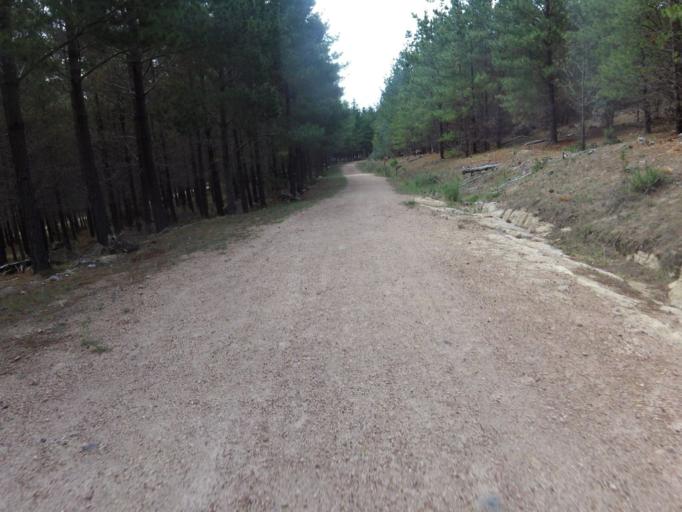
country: AU
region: Australian Capital Territory
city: Macarthur
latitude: -35.3798
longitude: 149.1200
